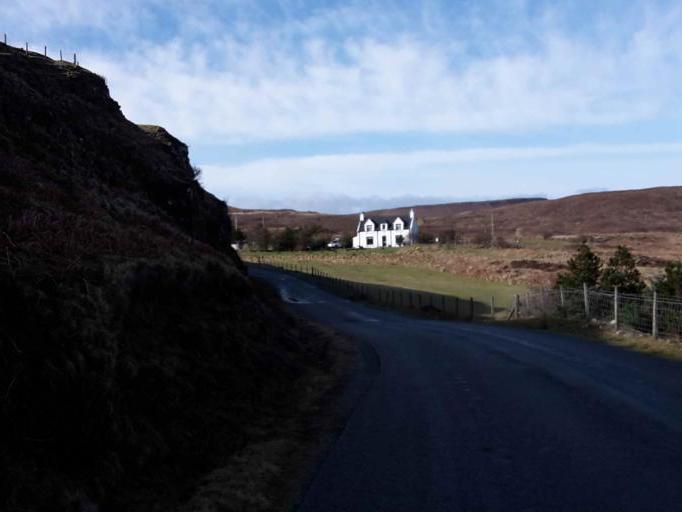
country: GB
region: Scotland
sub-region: Eilean Siar
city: Harris
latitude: 57.4471
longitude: -6.7195
